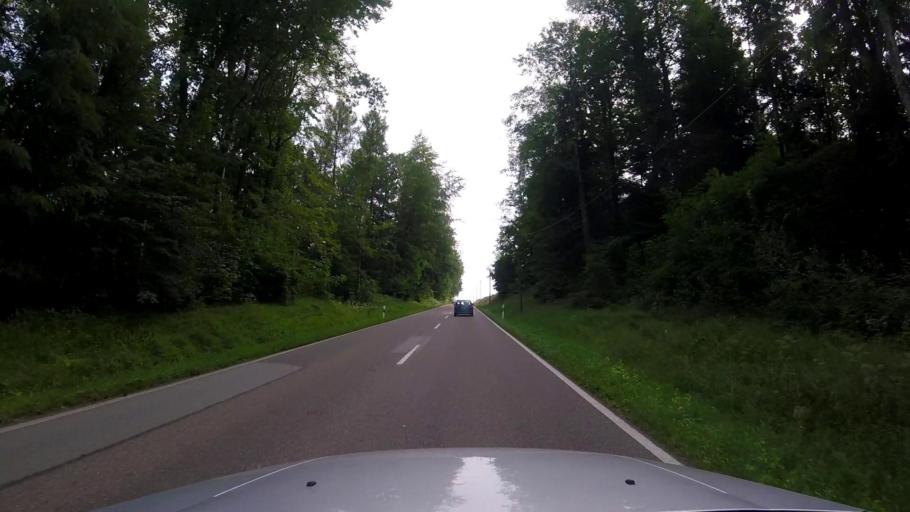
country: DE
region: Baden-Wuerttemberg
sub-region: Regierungsbezirk Stuttgart
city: Gschwend
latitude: 48.9091
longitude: 9.7445
